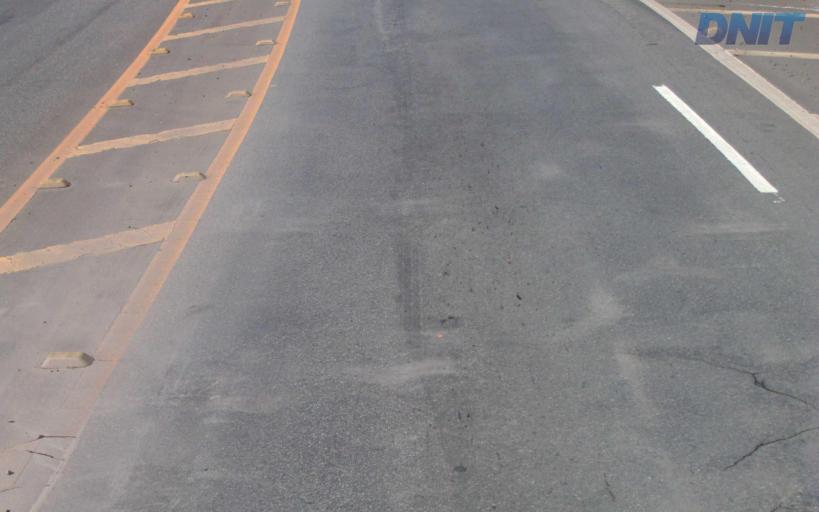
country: BR
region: Minas Gerais
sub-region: Ipaba
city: Ipaba
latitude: -19.3230
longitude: -42.4080
